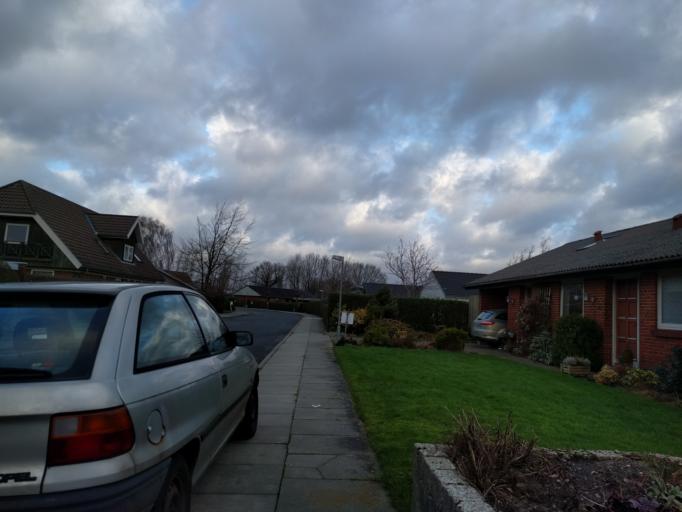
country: DK
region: Central Jutland
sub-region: Silkeborg Kommune
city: Silkeborg
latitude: 56.1916
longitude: 9.5218
